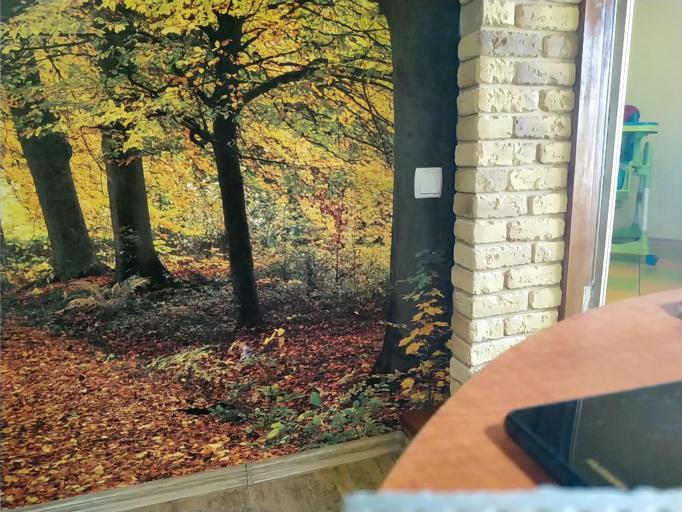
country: RU
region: Kaluga
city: Kondrovo
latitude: 54.8036
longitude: 35.9271
